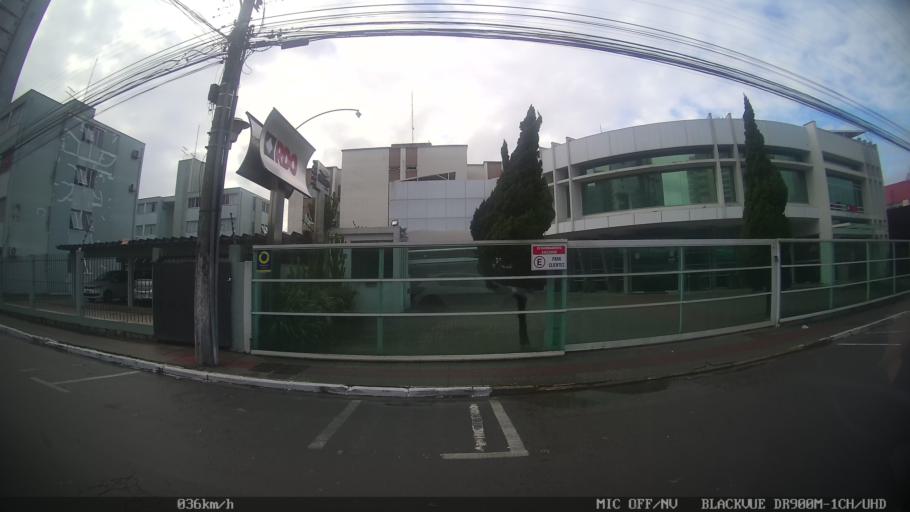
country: BR
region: Santa Catarina
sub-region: Sao Jose
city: Campinas
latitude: -27.5929
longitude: -48.6139
